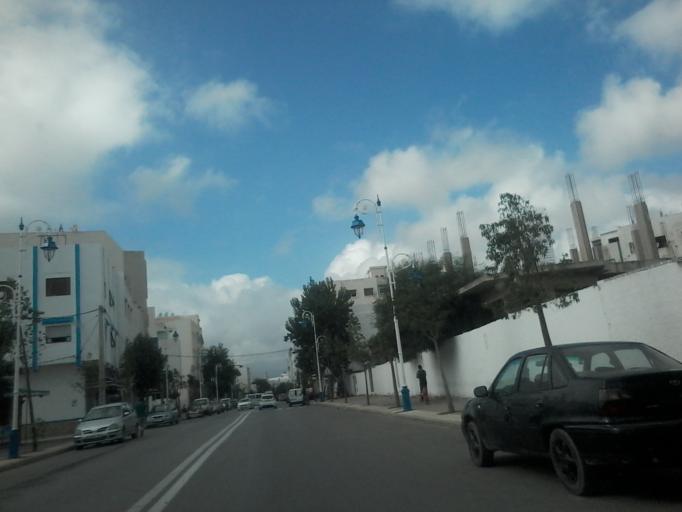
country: MA
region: Tanger-Tetouan
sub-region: Tetouan
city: Martil
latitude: 35.6262
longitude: -5.2771
